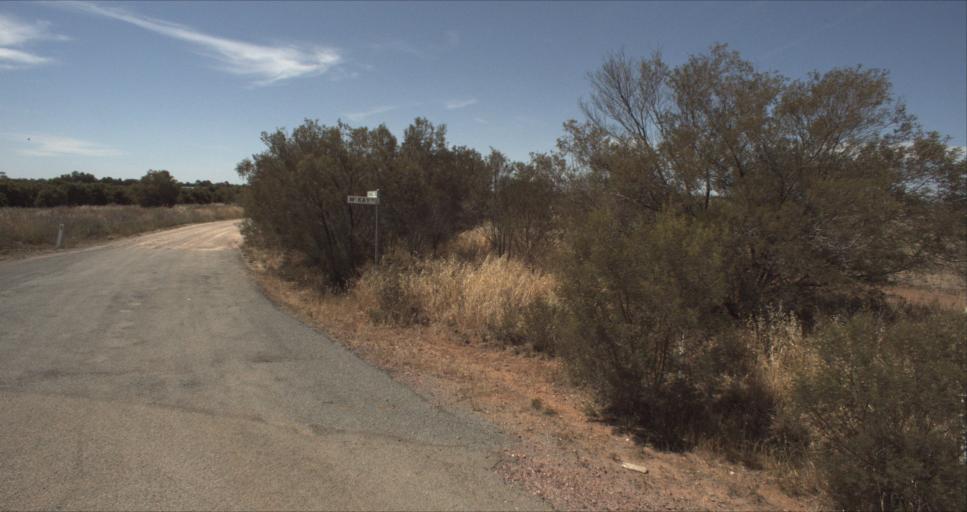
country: AU
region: New South Wales
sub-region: Leeton
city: Leeton
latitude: -34.6068
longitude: 146.4353
